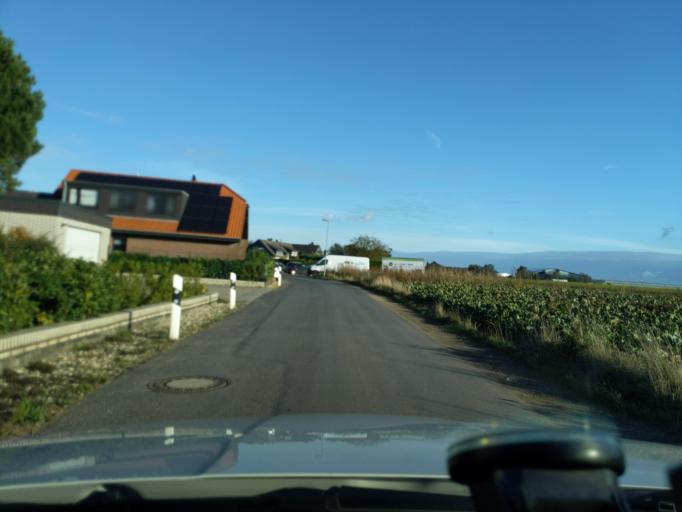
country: DE
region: North Rhine-Westphalia
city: Kempen
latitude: 51.3966
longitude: 6.4412
